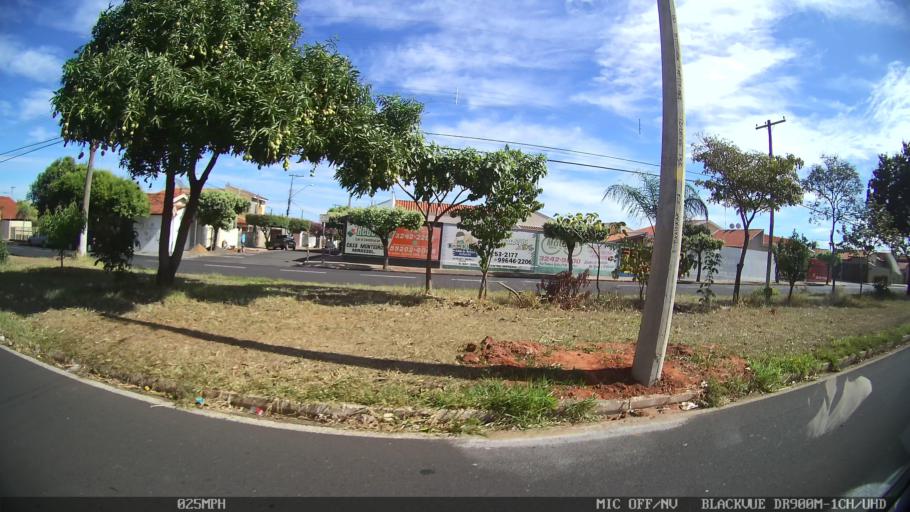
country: BR
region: Sao Paulo
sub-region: Bady Bassitt
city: Bady Bassitt
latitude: -20.8178
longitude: -49.4954
